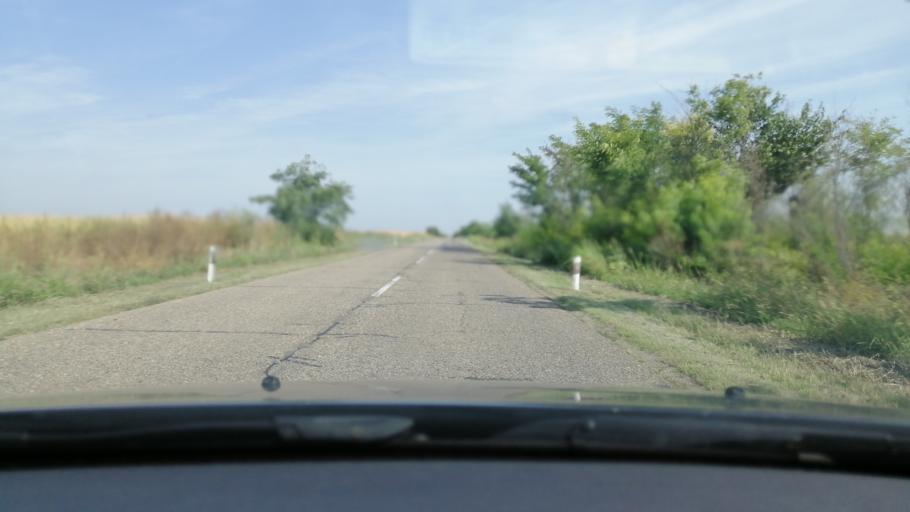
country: RS
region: Autonomna Pokrajina Vojvodina
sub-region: Juznobanatski Okrug
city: Kovacica
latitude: 45.1359
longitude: 20.6162
